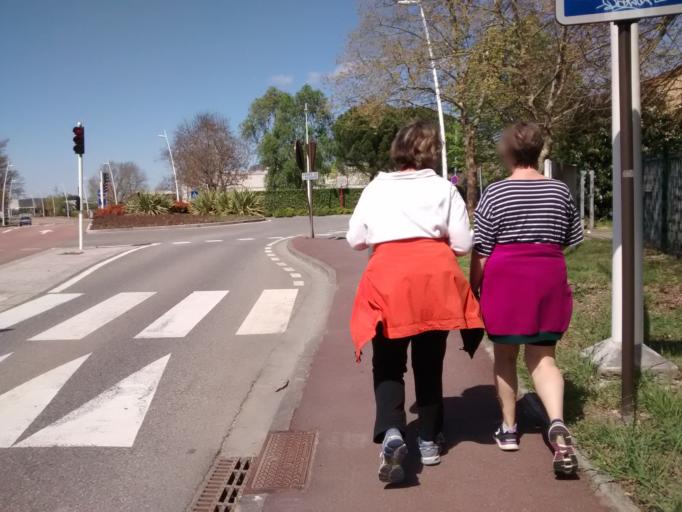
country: FR
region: Midi-Pyrenees
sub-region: Departement de la Haute-Garonne
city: Labege
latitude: 43.5385
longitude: 1.5162
